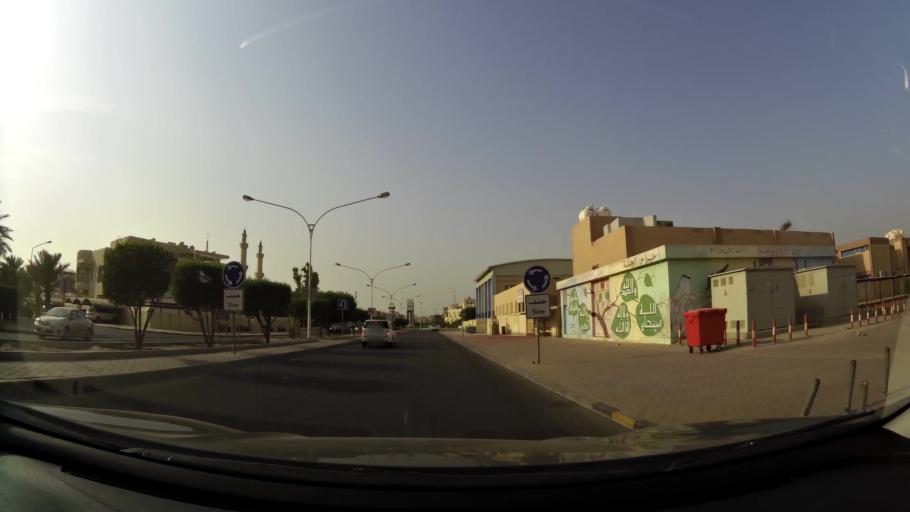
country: KW
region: Muhafazat Hawalli
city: Hawalli
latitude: 29.3119
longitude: 48.0066
